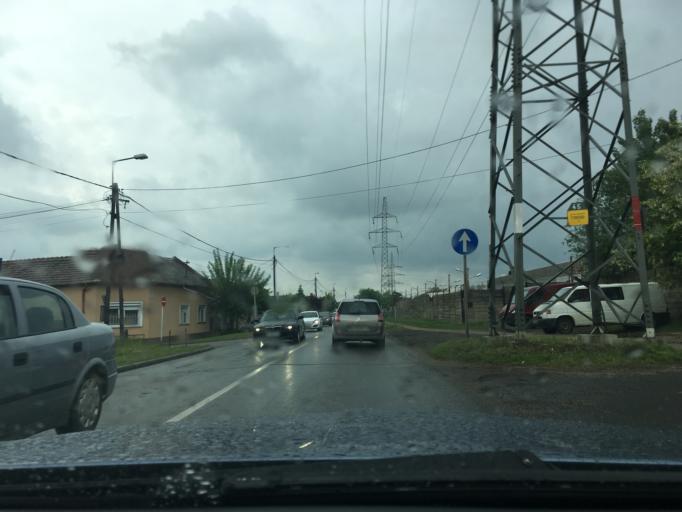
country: HU
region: Hajdu-Bihar
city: Debrecen
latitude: 47.5276
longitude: 21.6601
